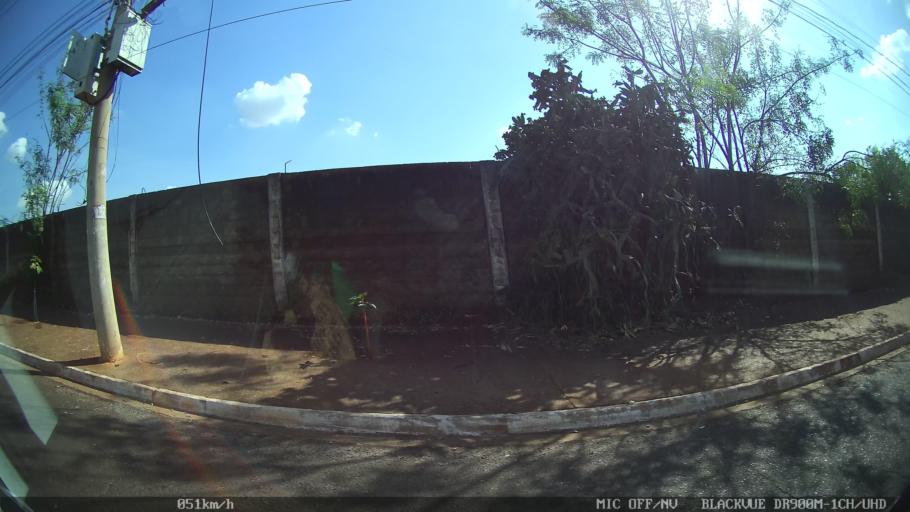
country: BR
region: Sao Paulo
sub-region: Ribeirao Preto
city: Ribeirao Preto
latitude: -21.1888
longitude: -47.8444
